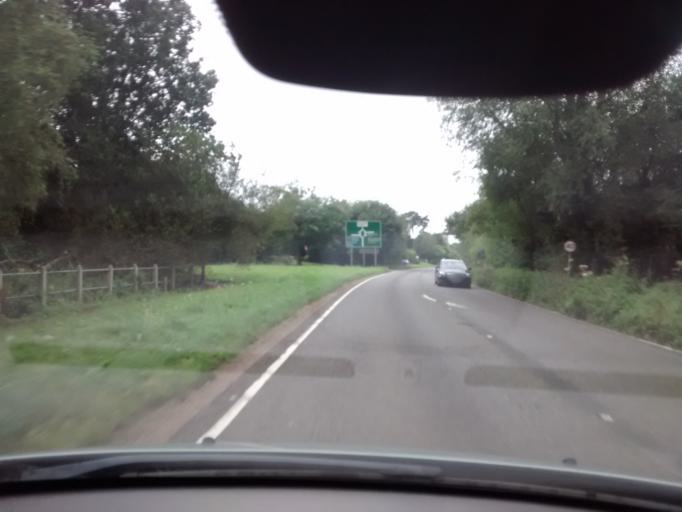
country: GB
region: England
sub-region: Hampshire
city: Ringwood
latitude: 50.8519
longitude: -1.7892
